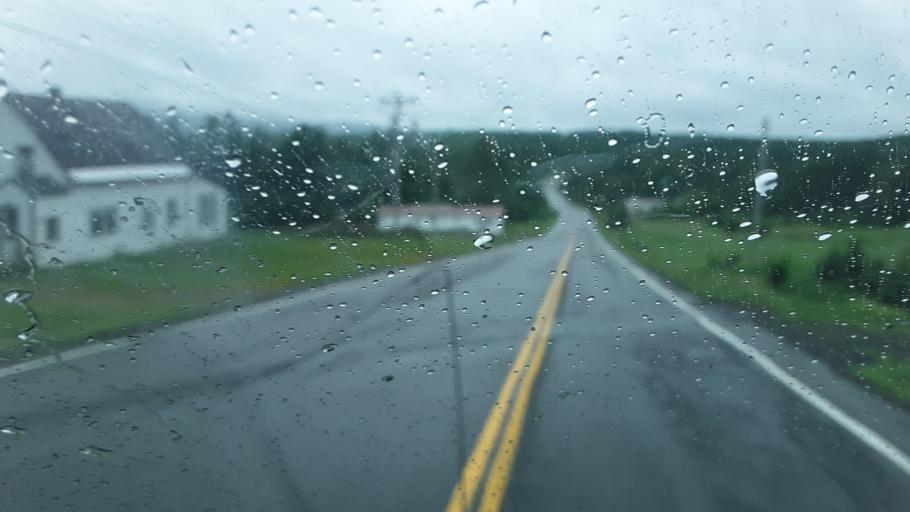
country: US
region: Maine
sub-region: Penobscot County
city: Patten
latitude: 46.0500
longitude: -68.4428
